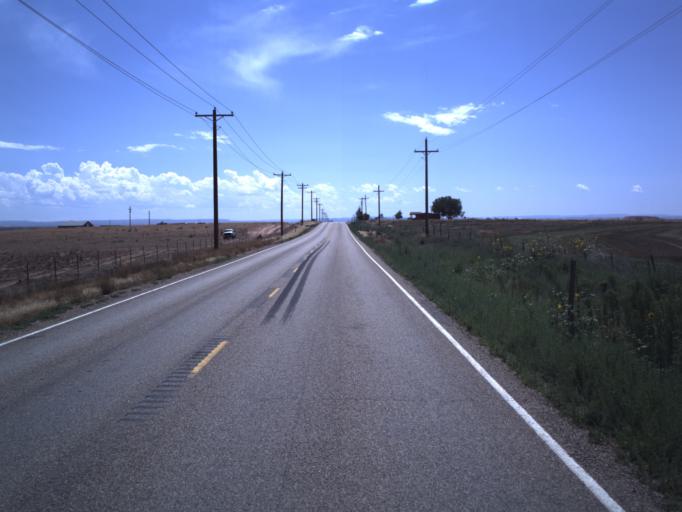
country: US
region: Utah
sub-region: Uintah County
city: Naples
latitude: 40.1703
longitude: -109.6645
